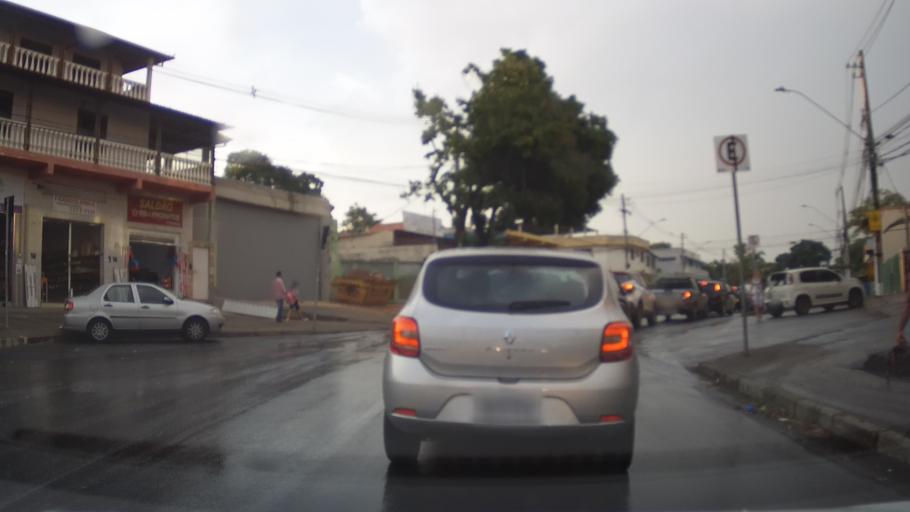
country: BR
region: Minas Gerais
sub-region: Belo Horizonte
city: Belo Horizonte
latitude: -19.9697
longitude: -43.9806
